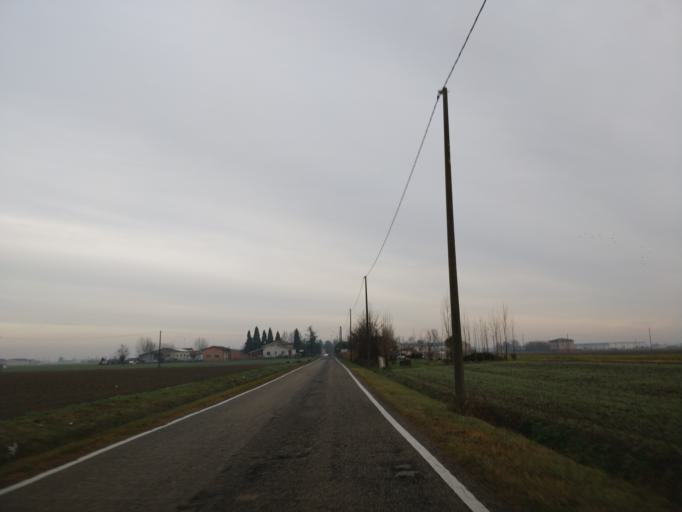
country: IT
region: Emilia-Romagna
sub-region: Provincia di Ferrara
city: Dosso
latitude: 44.7818
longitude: 11.3348
